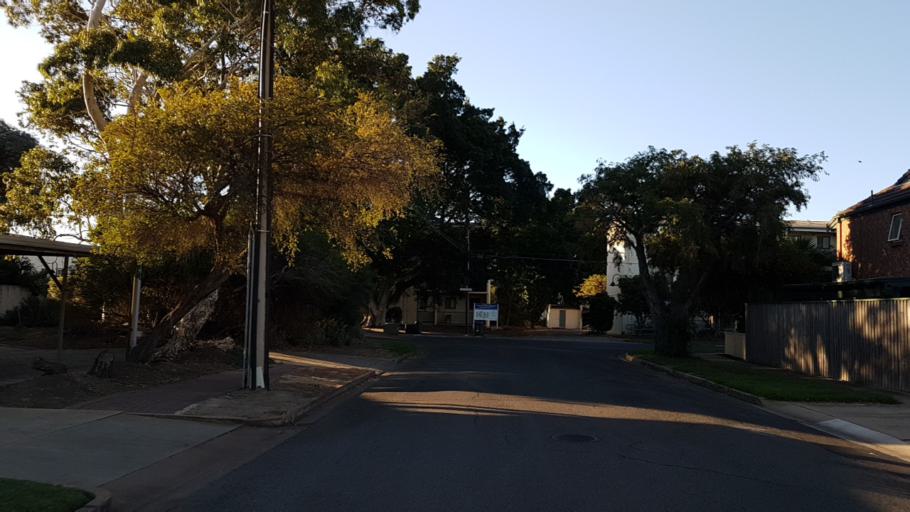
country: AU
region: South Australia
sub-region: Charles Sturt
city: Henley Beach
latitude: -34.9283
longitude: 138.5066
